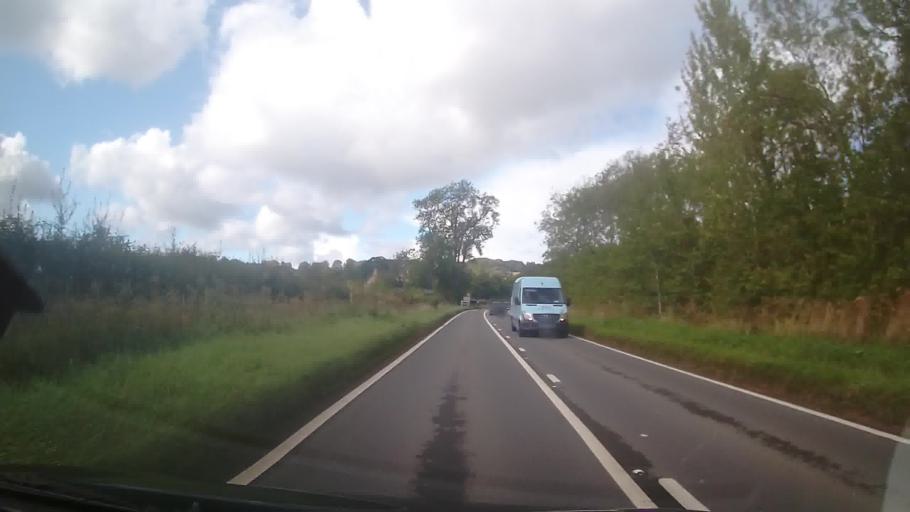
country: GB
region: England
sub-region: Gloucestershire
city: Moreton in Marsh
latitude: 51.9903
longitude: -1.7370
